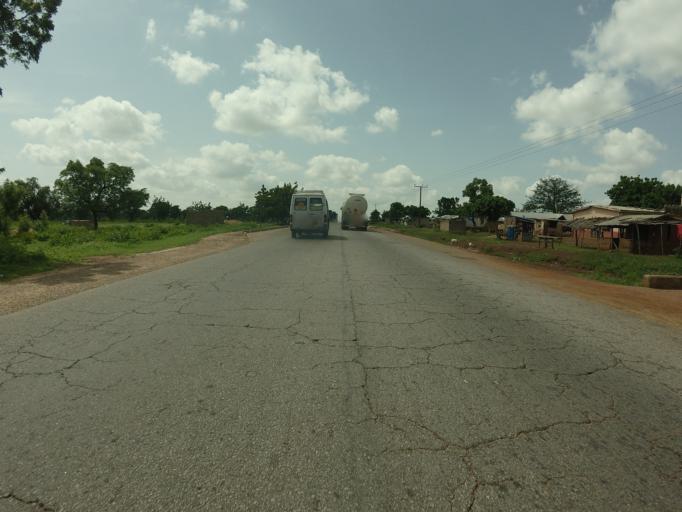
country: GH
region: Northern
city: Savelugu
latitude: 9.5782
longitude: -0.8340
